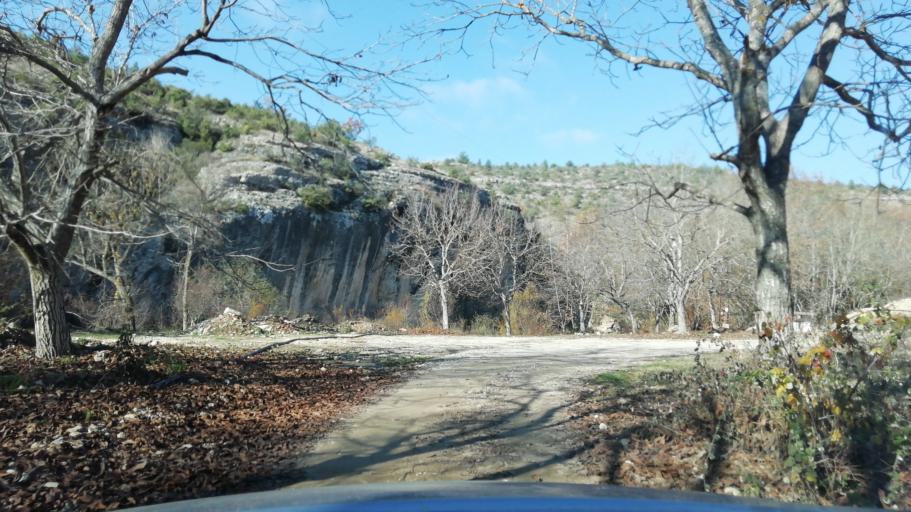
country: TR
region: Karabuk
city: Safranbolu
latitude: 41.2361
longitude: 32.7843
